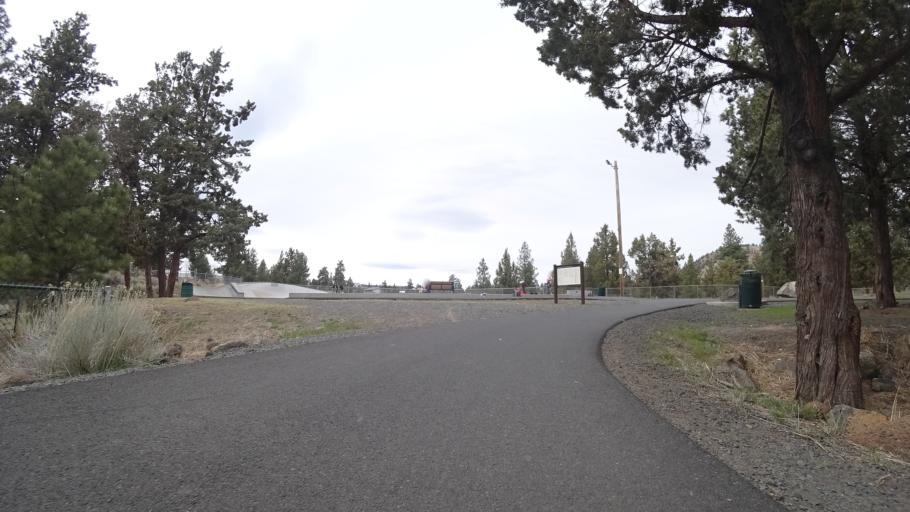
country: US
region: Oregon
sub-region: Deschutes County
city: Bend
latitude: 44.0478
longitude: -121.2857
